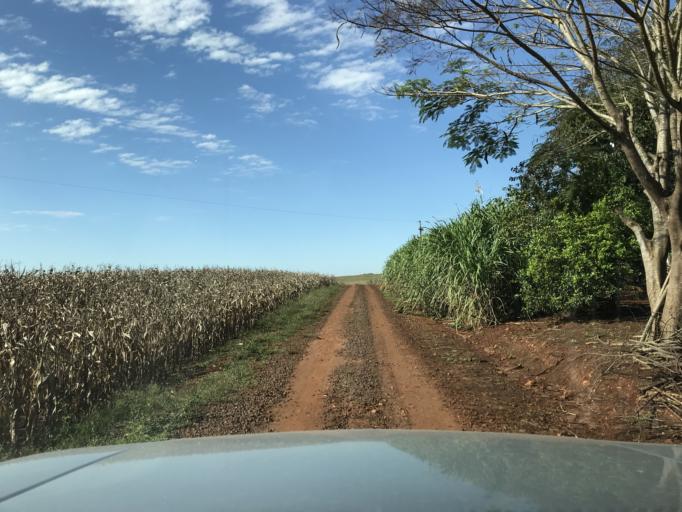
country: BR
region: Parana
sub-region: Ipora
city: Ipora
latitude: -24.1525
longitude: -53.7455
